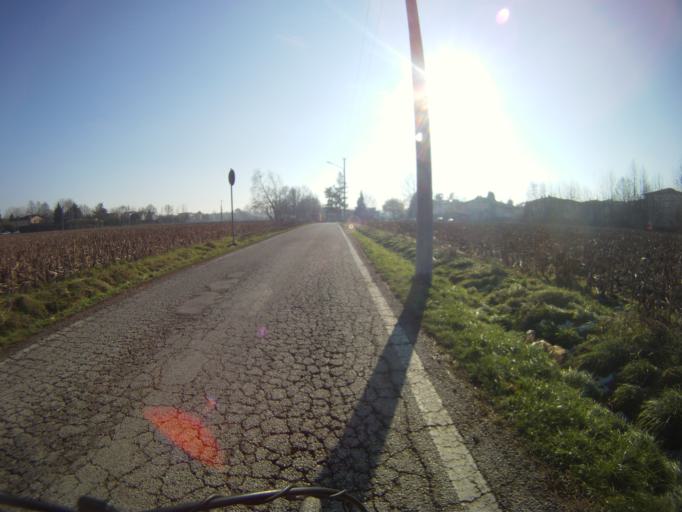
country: IT
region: Veneto
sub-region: Provincia di Padova
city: Mandriola-Sant'Agostino
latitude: 45.3905
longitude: 11.8588
